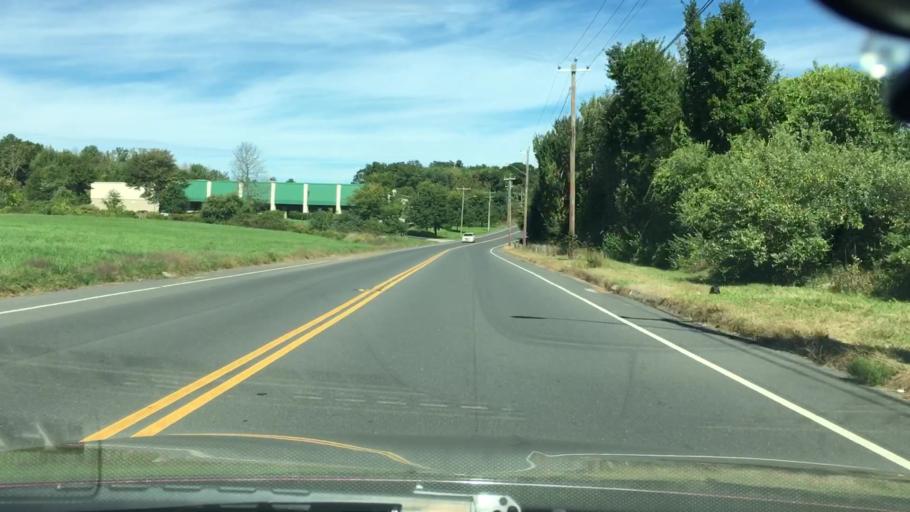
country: US
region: Connecticut
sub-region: Litchfield County
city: Terryville
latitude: 41.6880
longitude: -72.9842
